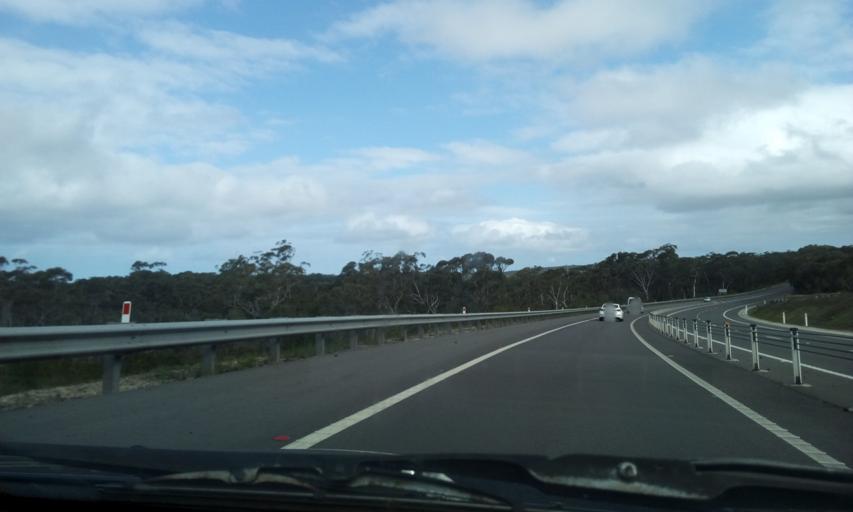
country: AU
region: New South Wales
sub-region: Wollongong
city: Bulli
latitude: -34.2677
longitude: 150.8952
